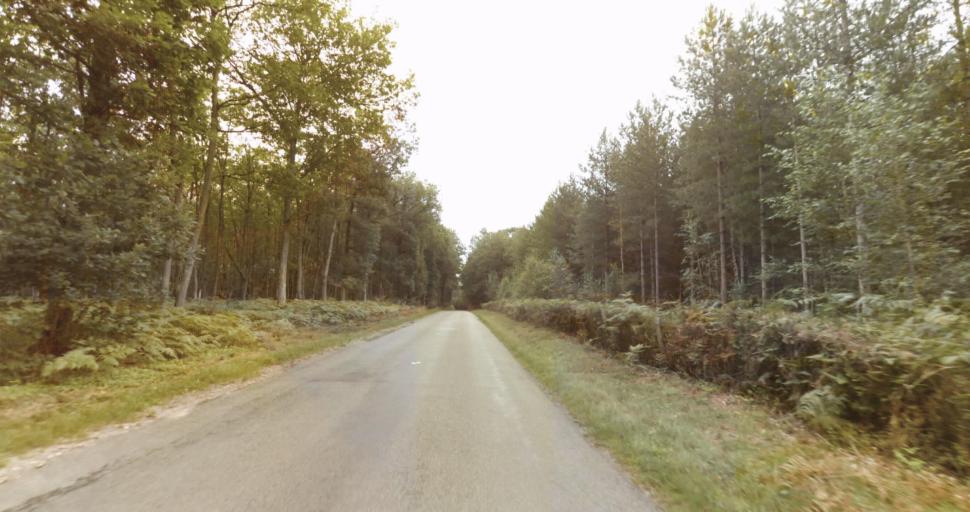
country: FR
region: Haute-Normandie
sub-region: Departement de l'Eure
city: La Couture-Boussey
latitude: 48.8864
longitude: 1.3658
